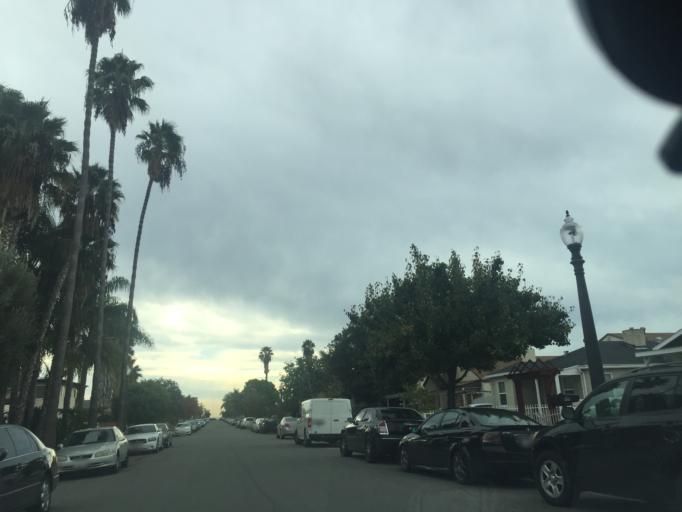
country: US
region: California
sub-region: San Diego County
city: Lemon Grove
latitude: 32.7603
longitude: -117.0846
